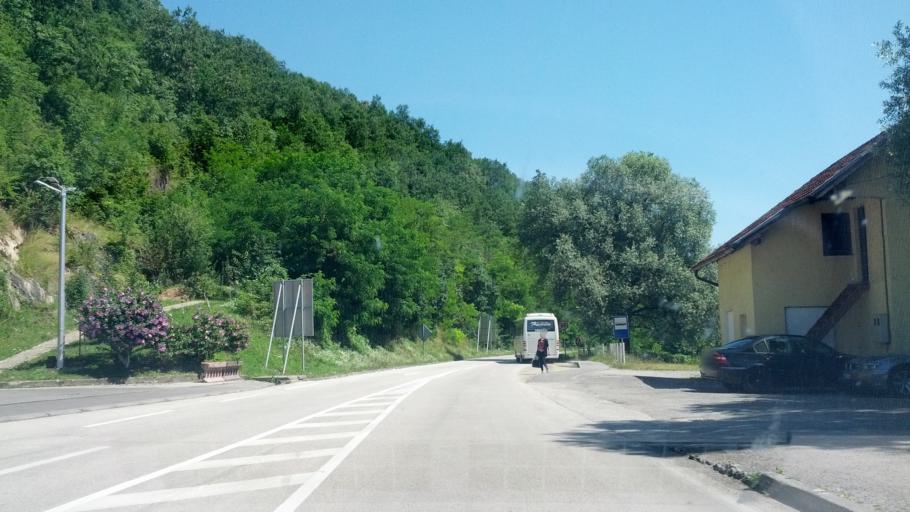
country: BA
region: Federation of Bosnia and Herzegovina
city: Otoka
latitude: 44.9411
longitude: 16.1623
